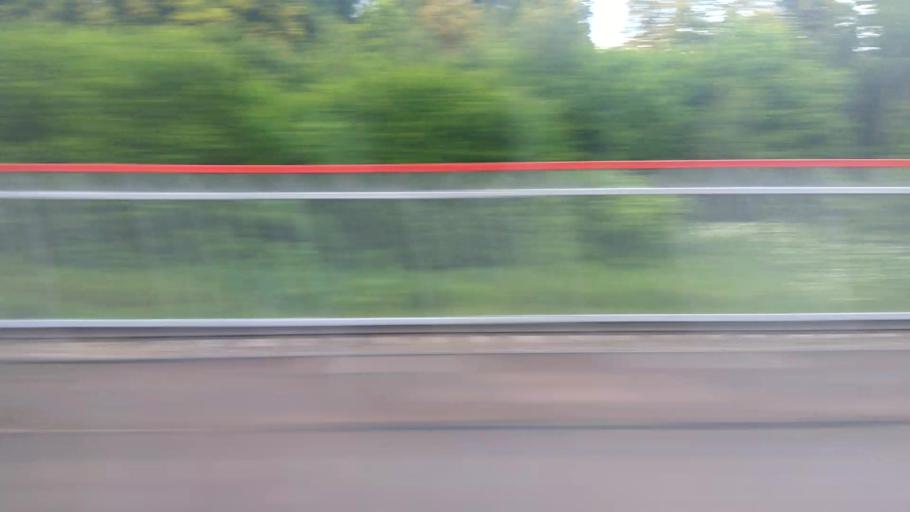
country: RU
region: Moskovskaya
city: Il'inskoye
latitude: 55.2038
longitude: 37.9214
